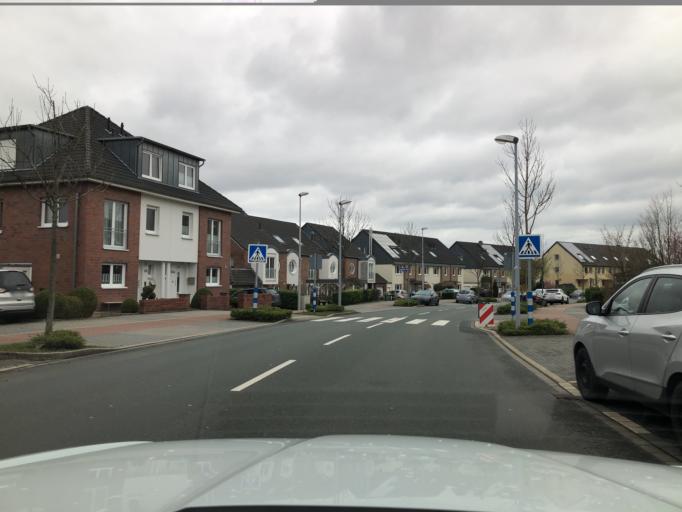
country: DE
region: North Rhine-Westphalia
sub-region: Regierungsbezirk Dusseldorf
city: Muelheim (Ruhr)
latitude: 51.3973
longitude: 6.8635
